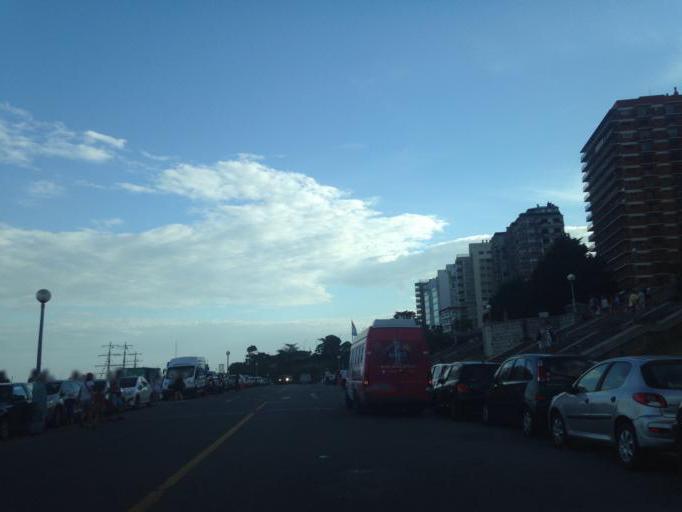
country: AR
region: Buenos Aires
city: Mar del Plata
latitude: -38.0275
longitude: -57.5329
